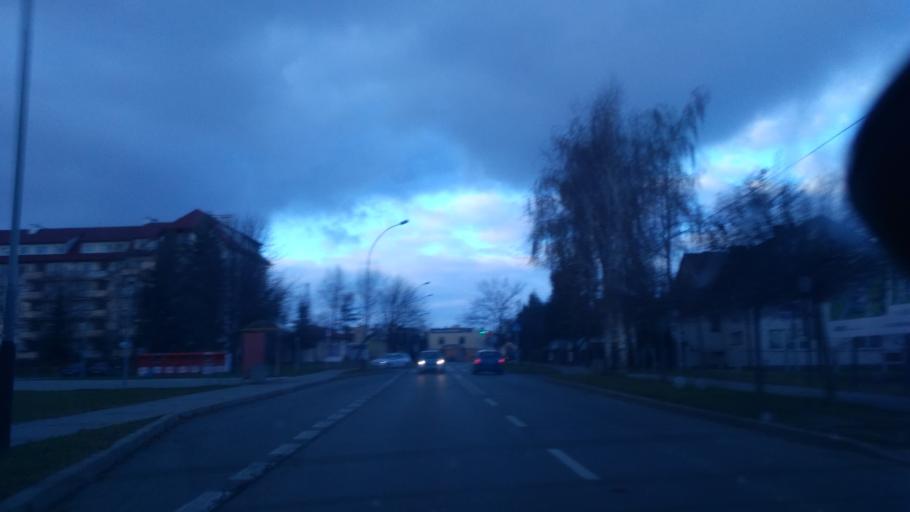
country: PL
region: Subcarpathian Voivodeship
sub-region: Rzeszow
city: Rzeszow
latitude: 50.0365
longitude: 22.0406
